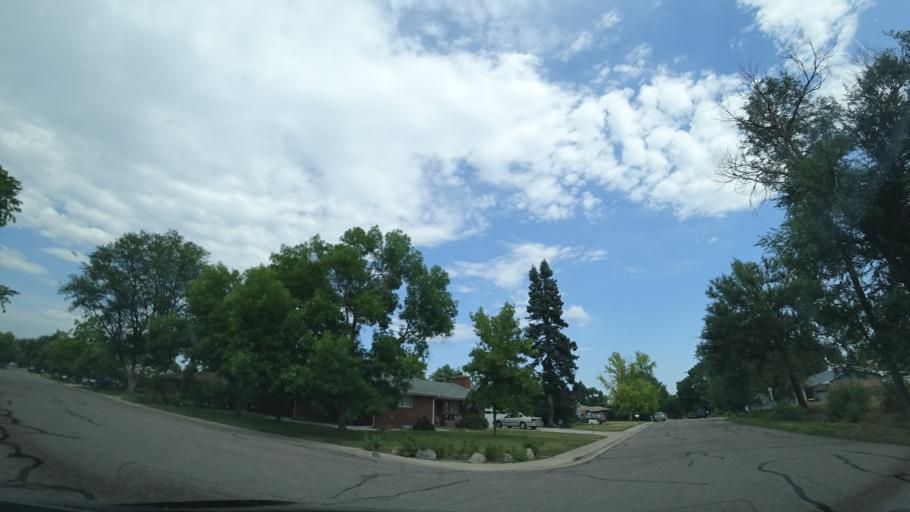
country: US
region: Colorado
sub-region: Jefferson County
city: Lakewood
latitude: 39.7217
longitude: -105.0674
